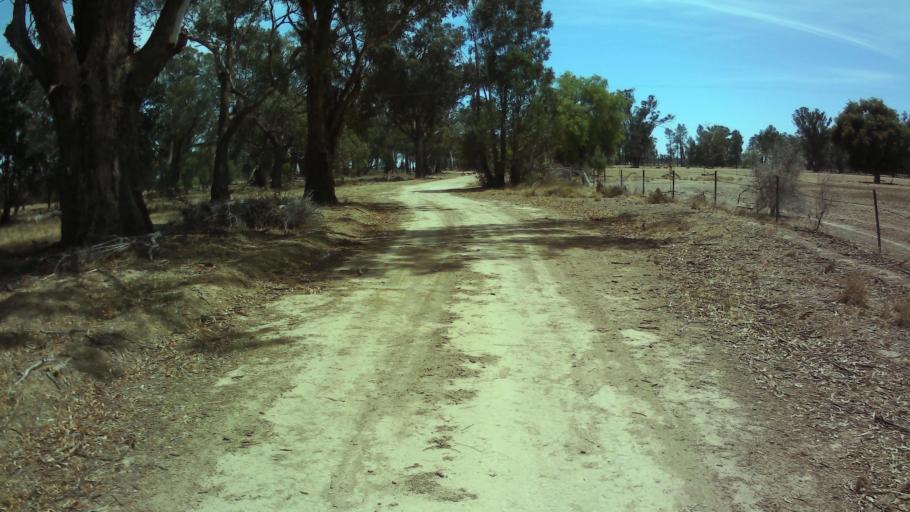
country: AU
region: New South Wales
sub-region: Weddin
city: Grenfell
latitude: -34.0349
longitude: 147.9346
